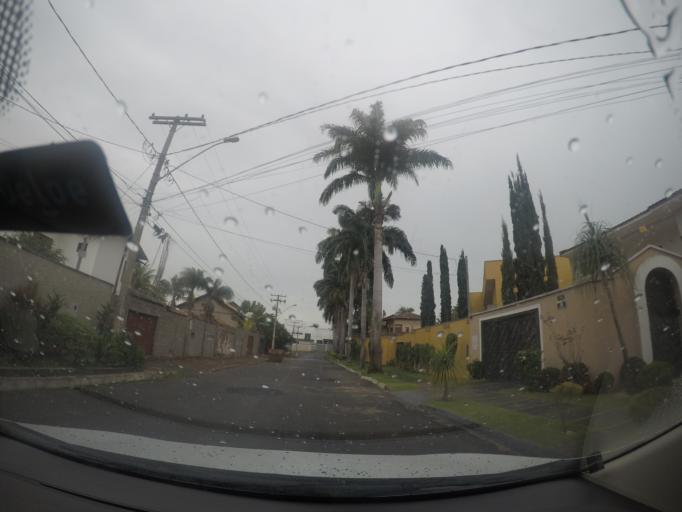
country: BR
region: Goias
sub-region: Goiania
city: Goiania
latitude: -16.6484
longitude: -49.2322
